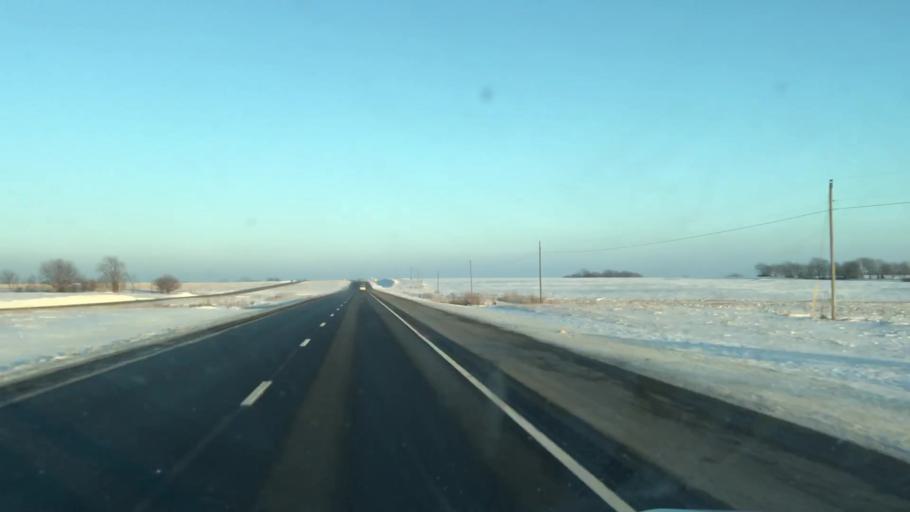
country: US
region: Missouri
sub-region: DeKalb County
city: Maysville
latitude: 39.7615
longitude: -94.3746
